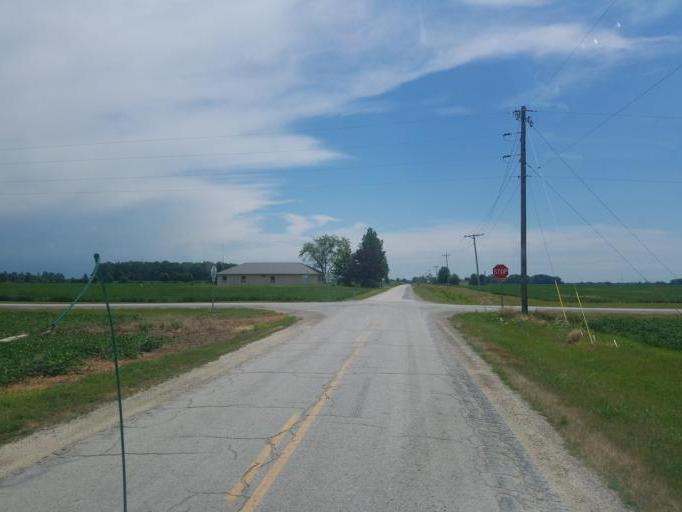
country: US
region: Ohio
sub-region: Paulding County
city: Antwerp
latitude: 41.2231
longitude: -84.7277
